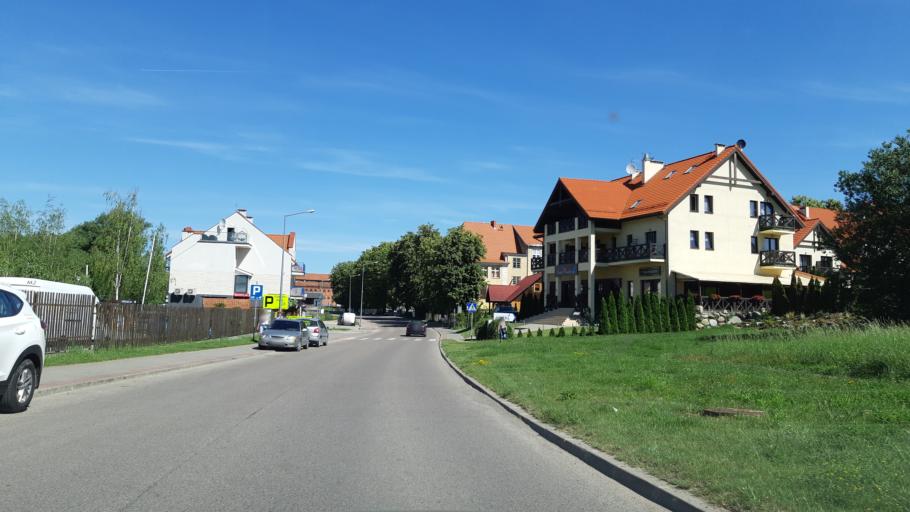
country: PL
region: Warmian-Masurian Voivodeship
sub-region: Powiat mragowski
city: Mikolajki
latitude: 53.8025
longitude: 21.5746
